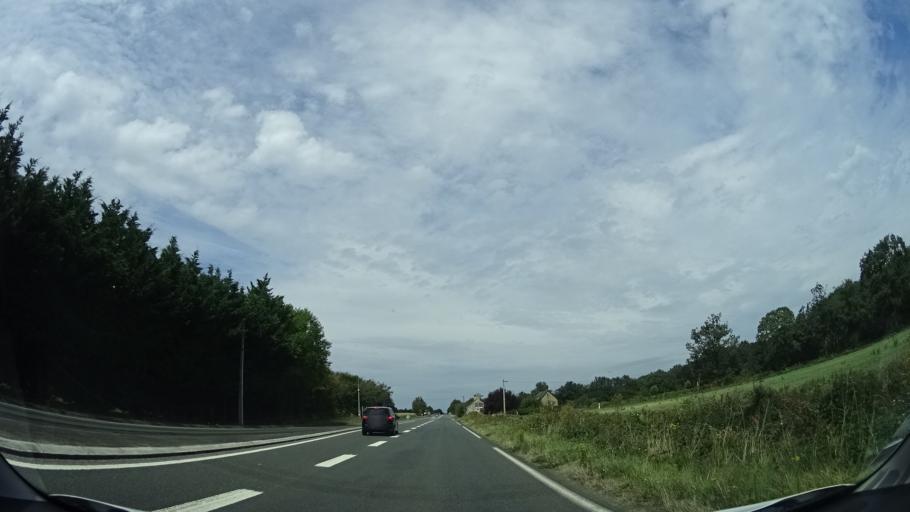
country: FR
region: Pays de la Loire
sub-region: Departement de la Sarthe
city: Vion
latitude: 47.7641
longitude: -0.1887
